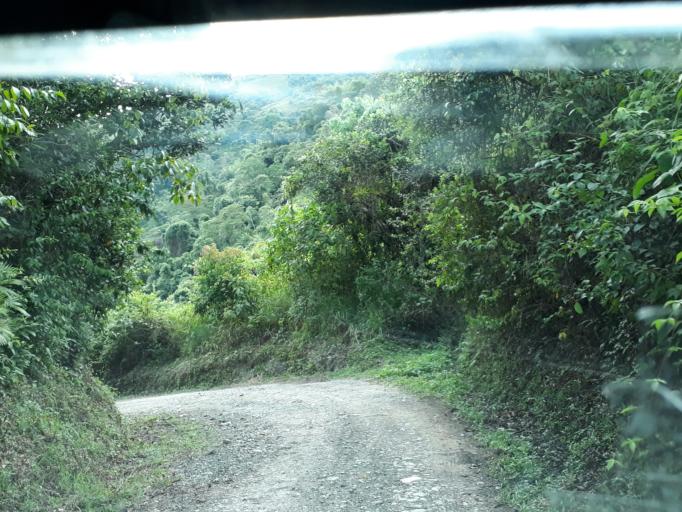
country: CO
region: Cundinamarca
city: Topaipi
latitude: 5.2767
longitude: -74.3536
